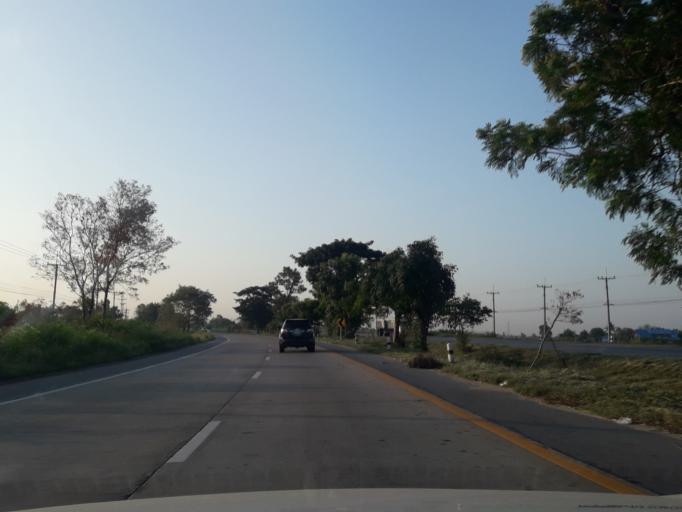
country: TH
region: Phra Nakhon Si Ayutthaya
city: Phra Nakhon Si Ayutthaya
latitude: 14.2922
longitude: 100.5243
